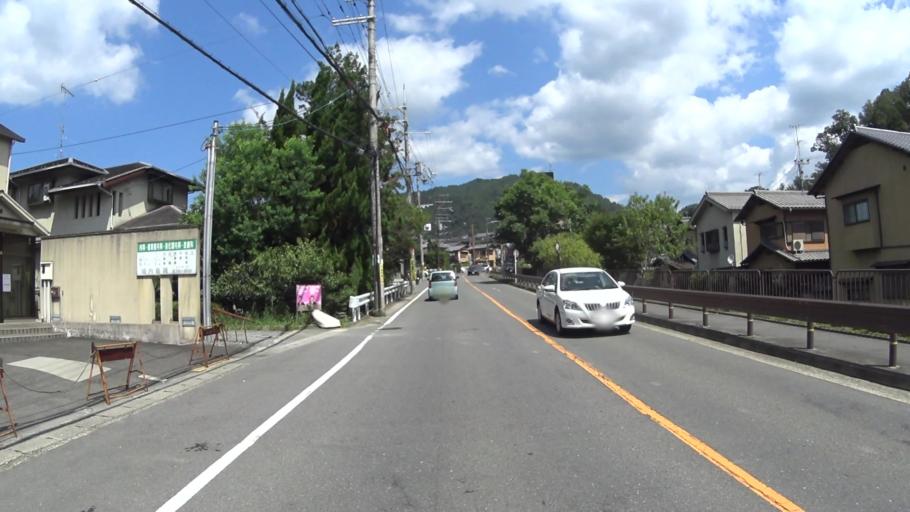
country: JP
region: Kyoto
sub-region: Kyoto-shi
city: Kamigyo-ku
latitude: 35.0822
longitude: 135.7621
